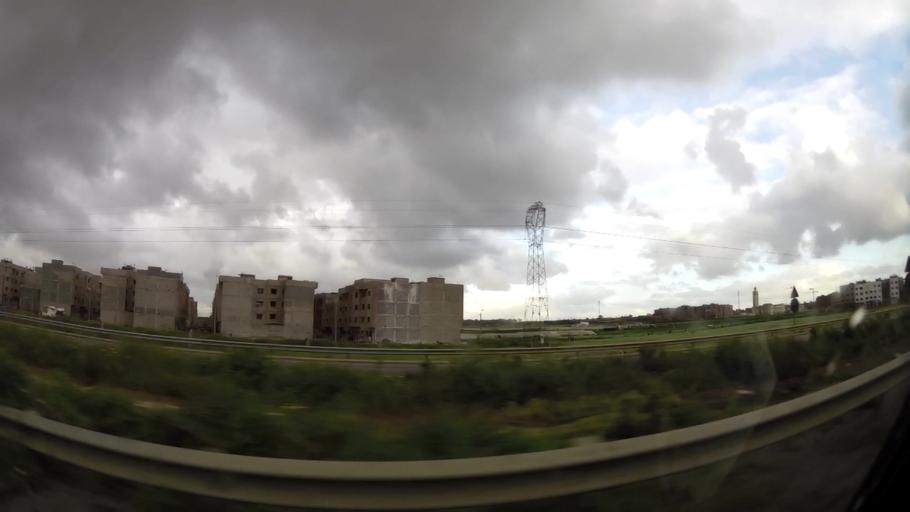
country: MA
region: Grand Casablanca
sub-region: Mohammedia
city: Mohammedia
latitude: 33.6425
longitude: -7.4216
